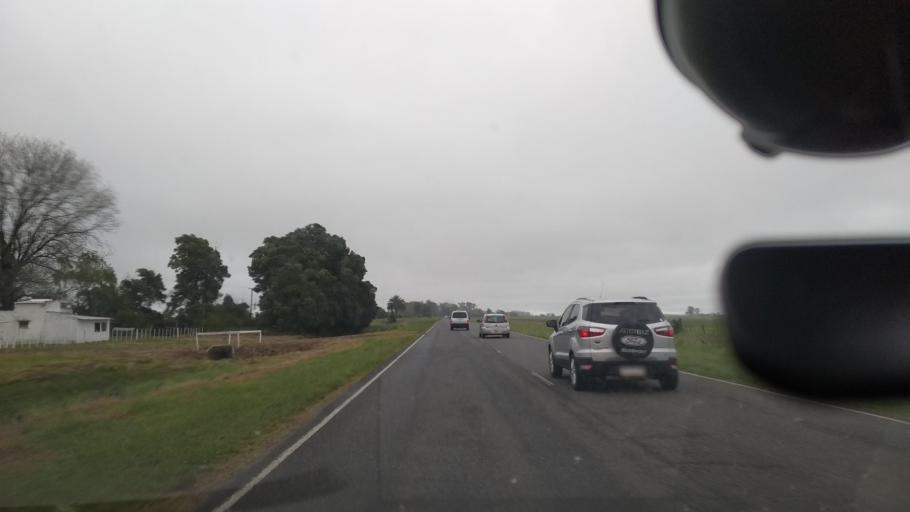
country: AR
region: Buenos Aires
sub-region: Partido de Magdalena
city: Magdalena
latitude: -35.2169
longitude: -57.7450
